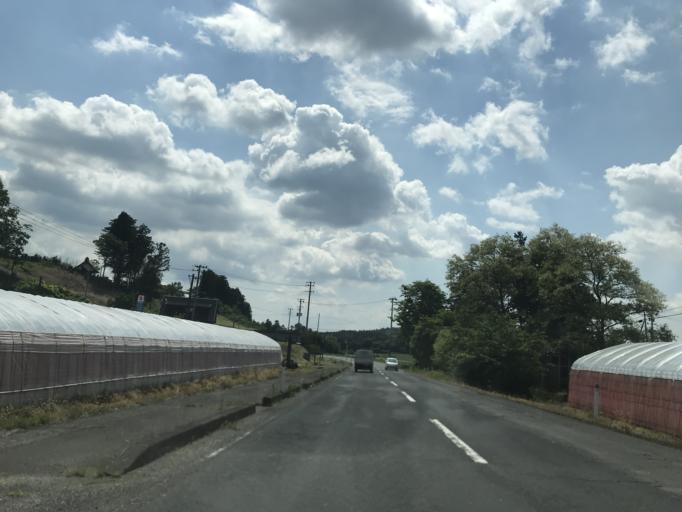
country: JP
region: Miyagi
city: Furukawa
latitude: 38.6847
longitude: 140.9557
